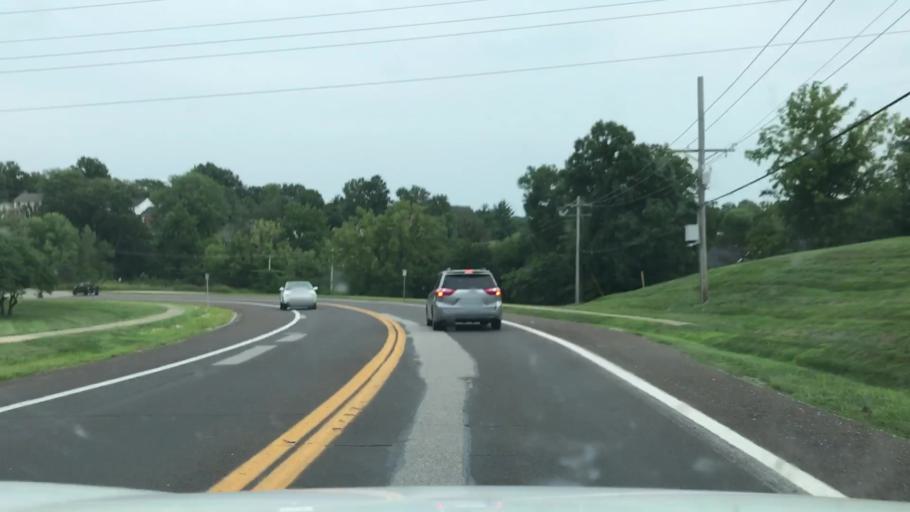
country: US
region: Missouri
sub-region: Saint Louis County
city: Clarkson Valley
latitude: 38.6248
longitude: -90.5909
